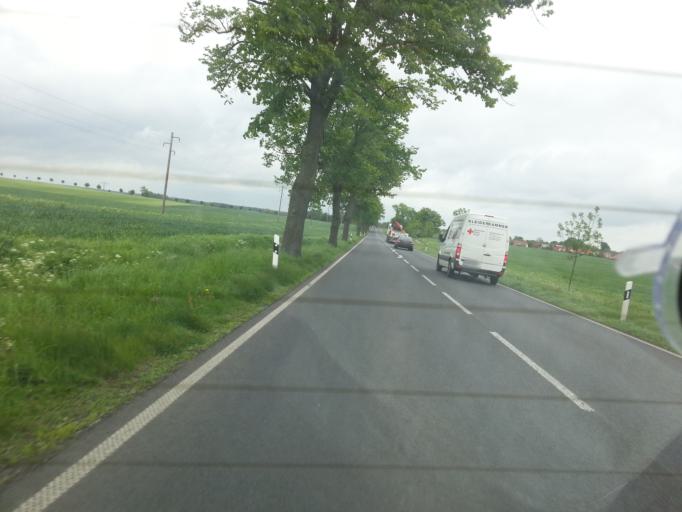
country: DE
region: Mecklenburg-Vorpommern
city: Klink
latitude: 53.4704
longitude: 12.6128
